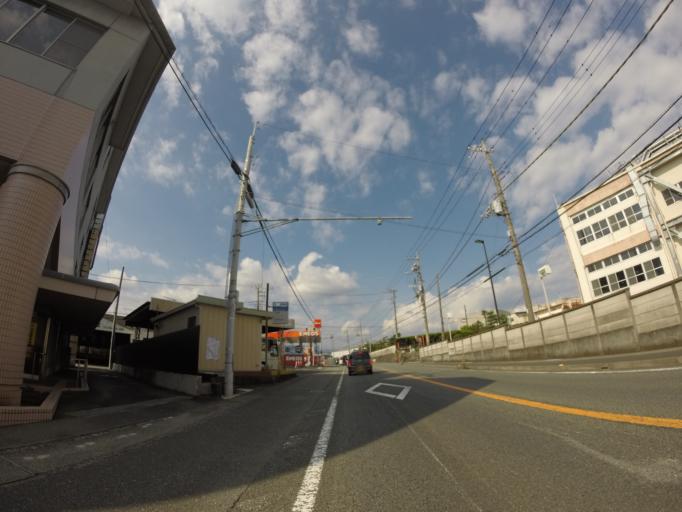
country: JP
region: Shizuoka
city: Fujinomiya
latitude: 35.2201
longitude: 138.6209
